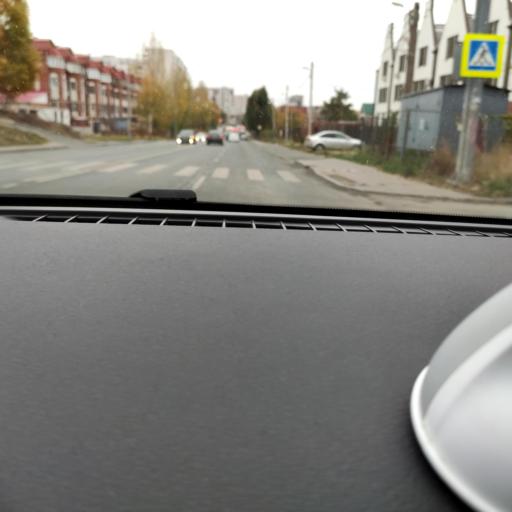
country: RU
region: Samara
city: Samara
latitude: 53.2690
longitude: 50.2153
